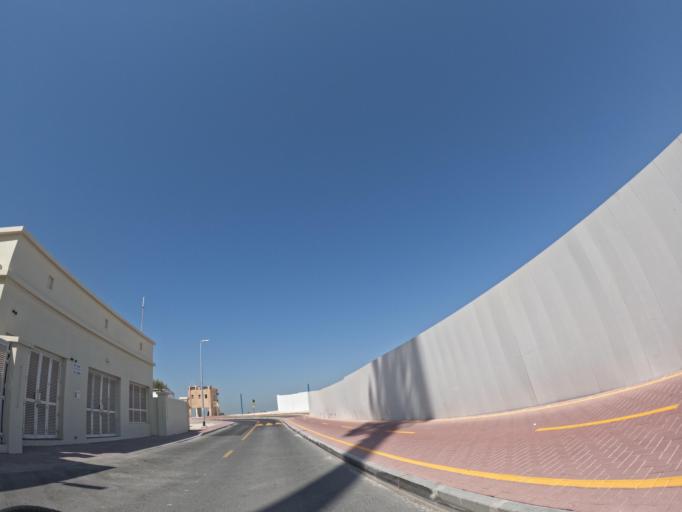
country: AE
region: Dubai
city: Dubai
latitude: 25.1929
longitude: 55.2318
